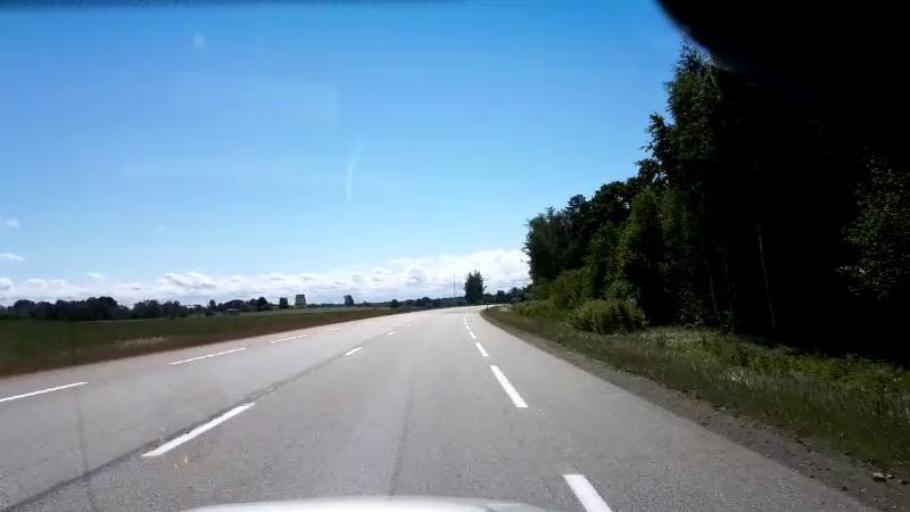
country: LV
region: Saulkrastu
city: Saulkrasti
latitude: 57.4090
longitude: 24.4321
